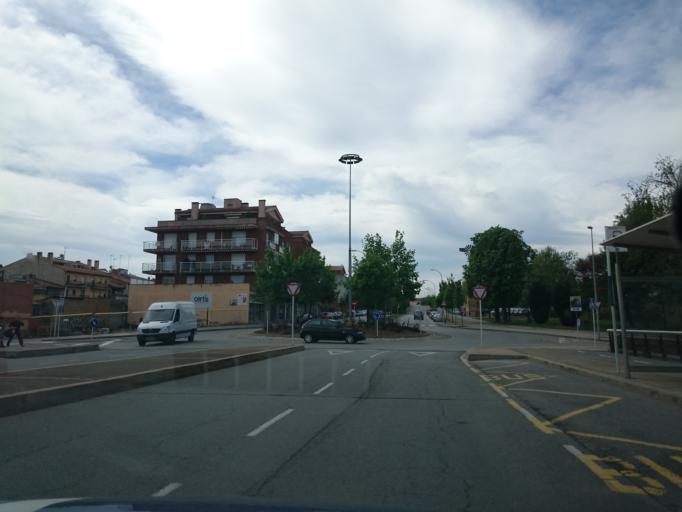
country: ES
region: Catalonia
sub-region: Provincia de Barcelona
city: Vic
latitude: 41.9247
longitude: 2.2488
